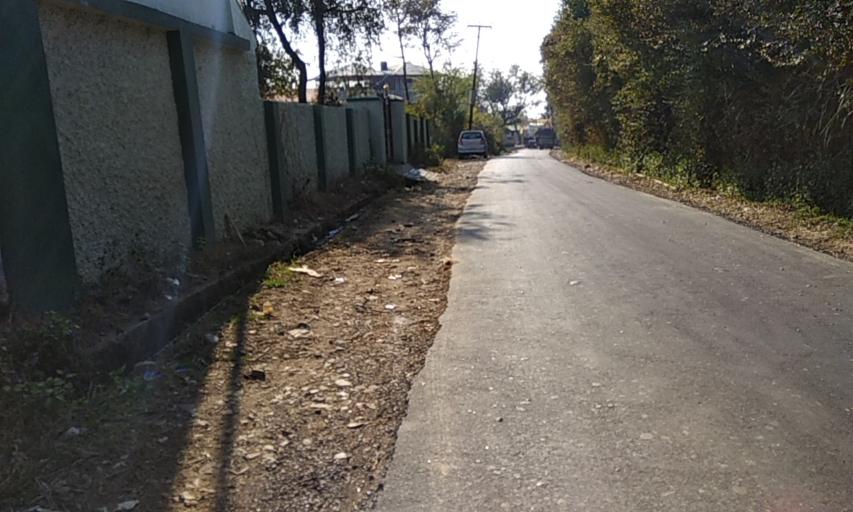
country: IN
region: Himachal Pradesh
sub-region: Kangra
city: Palampur
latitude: 32.1145
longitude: 76.5238
